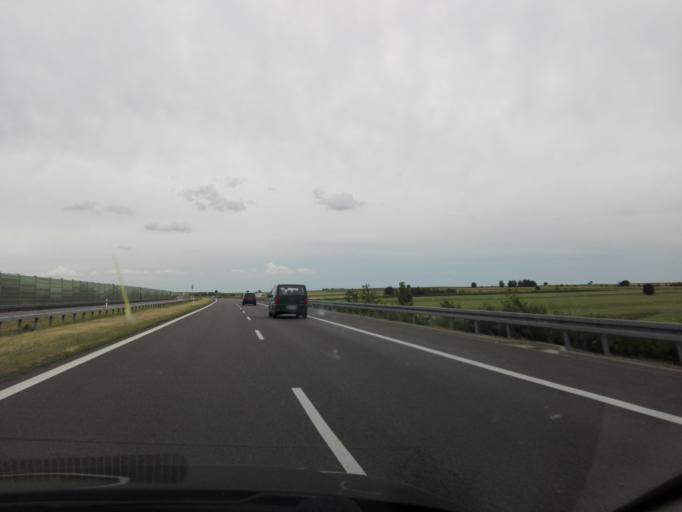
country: PL
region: Lublin Voivodeship
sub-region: Powiat pulawski
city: Kurow
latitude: 51.3950
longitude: 22.2244
